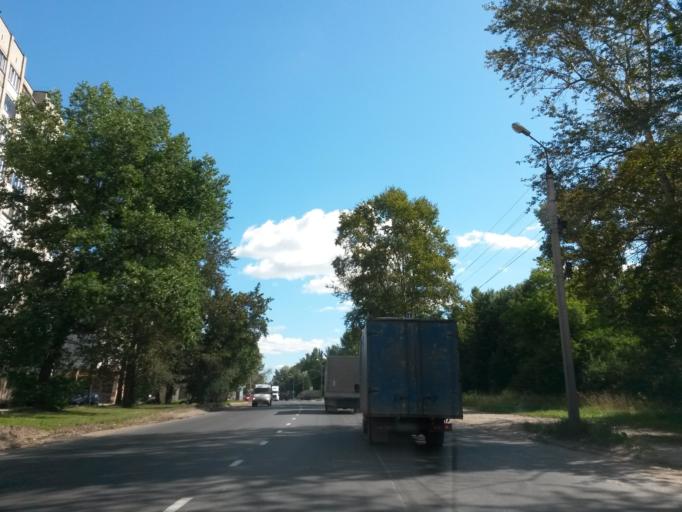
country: RU
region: Jaroslavl
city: Yaroslavl
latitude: 57.5840
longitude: 39.8238
